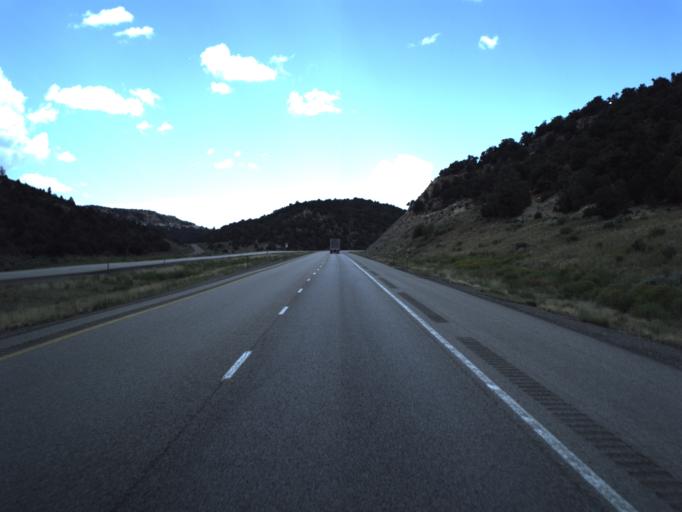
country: US
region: Utah
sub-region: Wayne County
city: Loa
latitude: 38.7643
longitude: -111.4654
